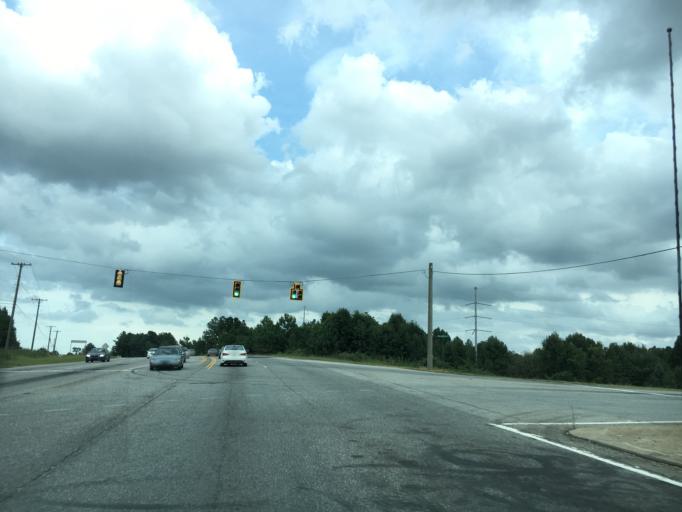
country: US
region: South Carolina
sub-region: Greenville County
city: Greer
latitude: 34.9040
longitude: -82.1924
